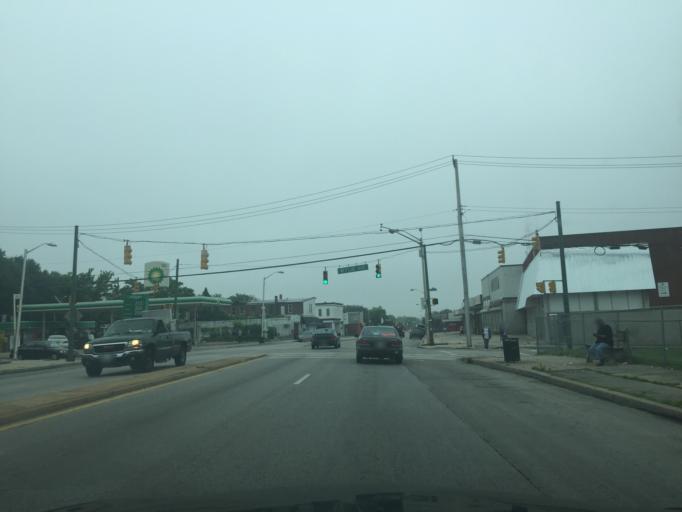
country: US
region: Maryland
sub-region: Baltimore County
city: Lochearn
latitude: 39.3414
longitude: -76.6679
